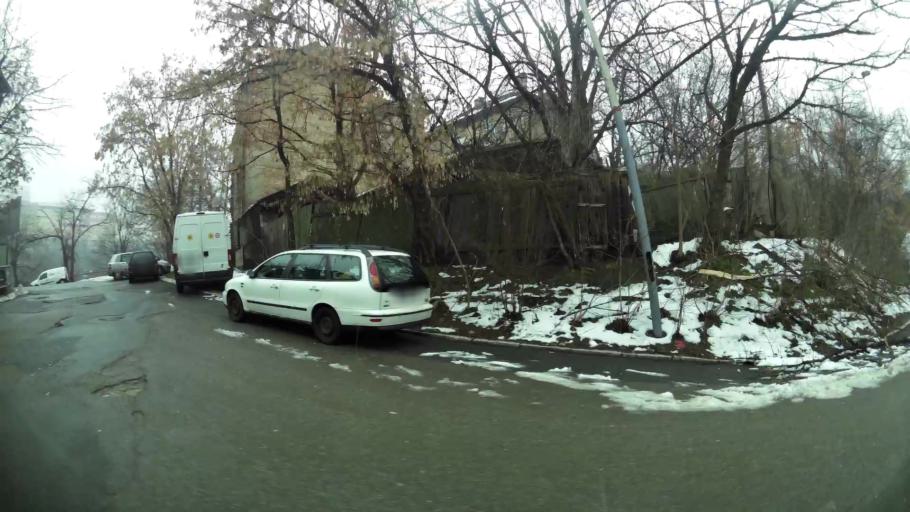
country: RS
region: Central Serbia
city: Belgrade
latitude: 44.7952
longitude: 20.4537
